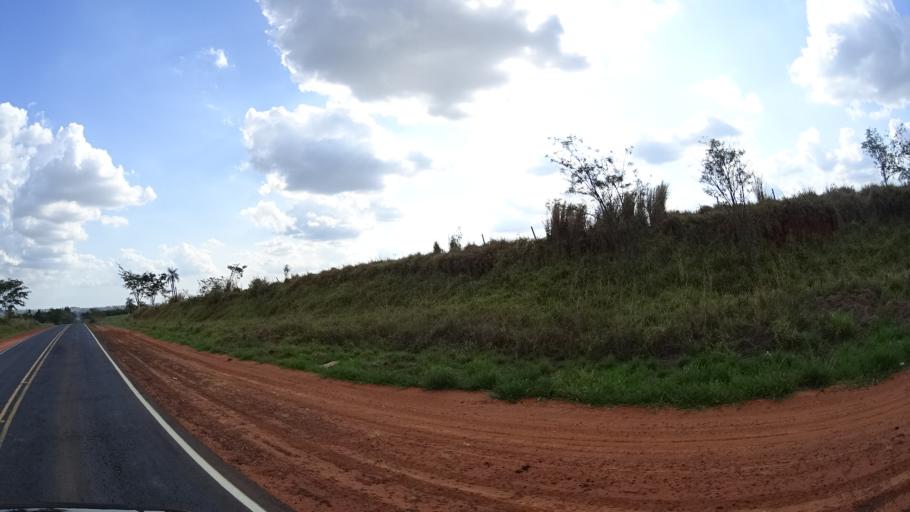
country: BR
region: Sao Paulo
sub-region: Urupes
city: Urupes
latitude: -21.1070
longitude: -49.2652
